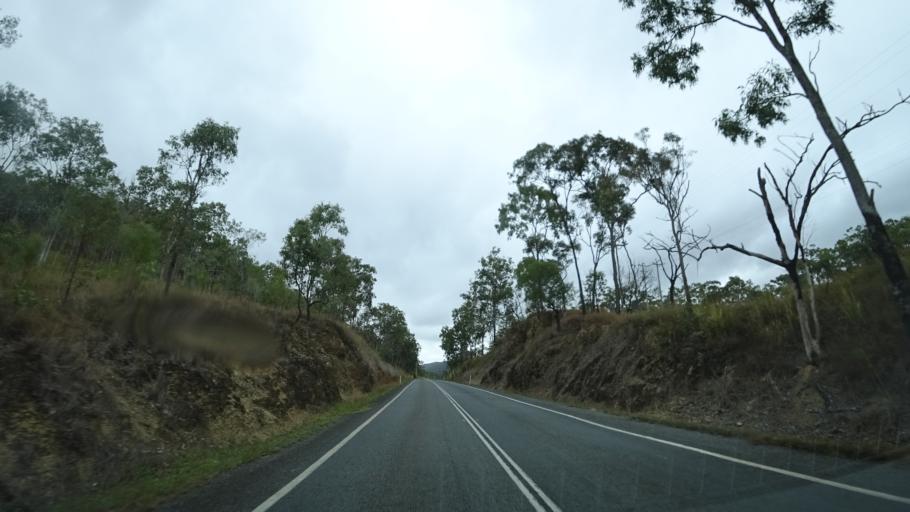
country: AU
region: Queensland
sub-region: Cairns
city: Port Douglas
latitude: -16.7062
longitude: 145.3484
